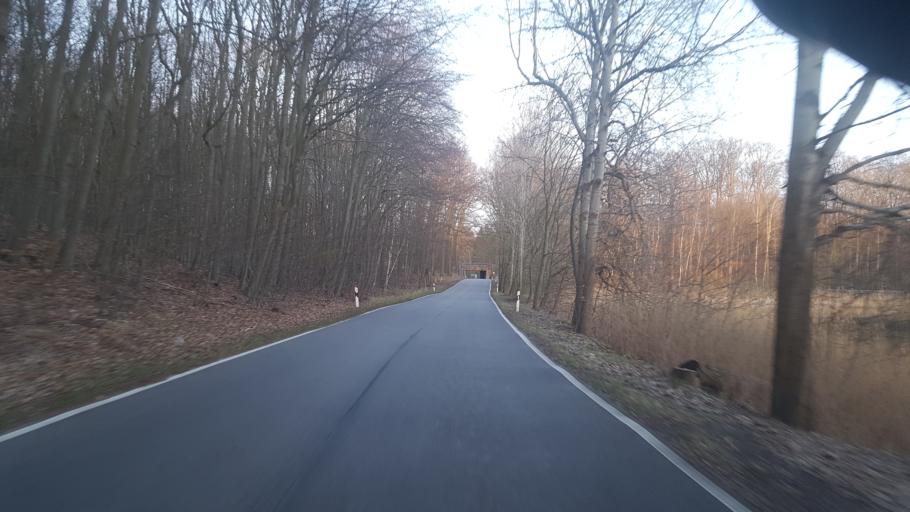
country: DE
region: Brandenburg
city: Gramzow
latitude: 53.1869
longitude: 13.9284
